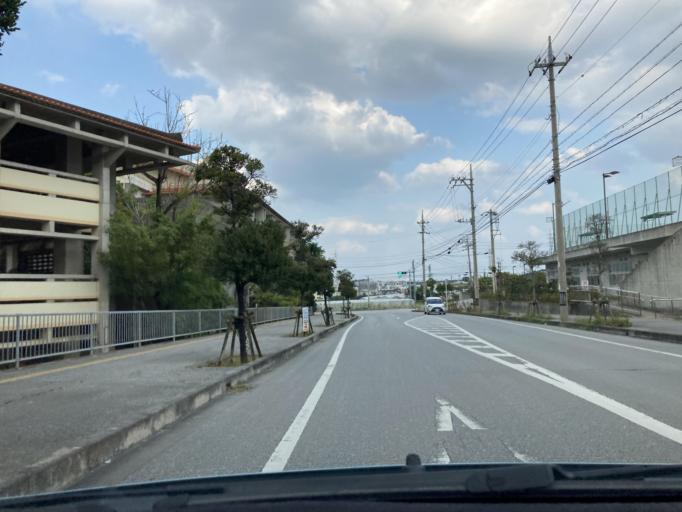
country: JP
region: Okinawa
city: Tomigusuku
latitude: 26.1919
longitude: 127.7321
